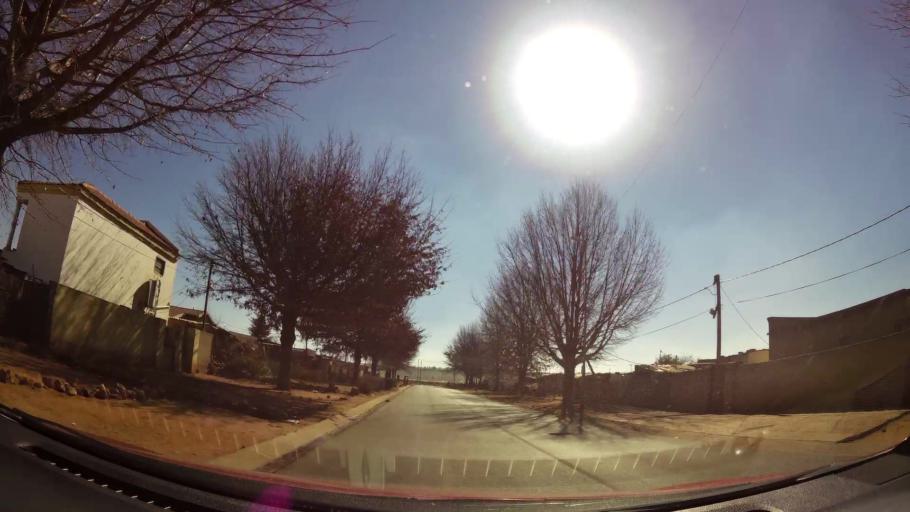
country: ZA
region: Gauteng
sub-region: City of Johannesburg Metropolitan Municipality
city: Soweto
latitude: -26.2168
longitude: 27.8326
